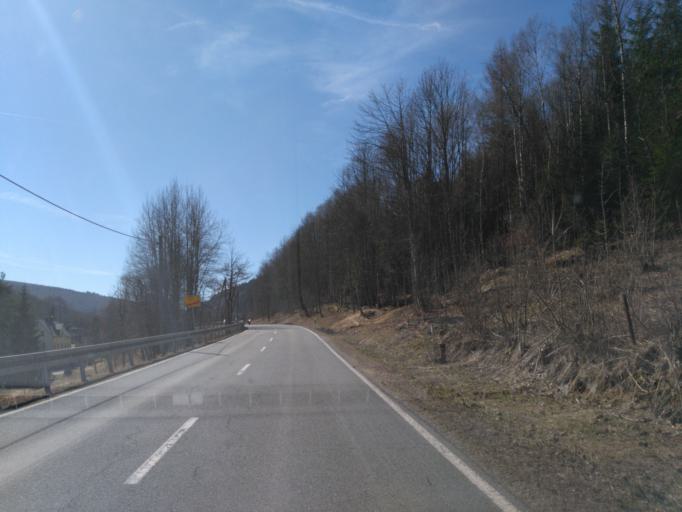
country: CZ
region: Ustecky
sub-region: Okres Chomutov
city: Vejprty
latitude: 50.4639
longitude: 13.0185
